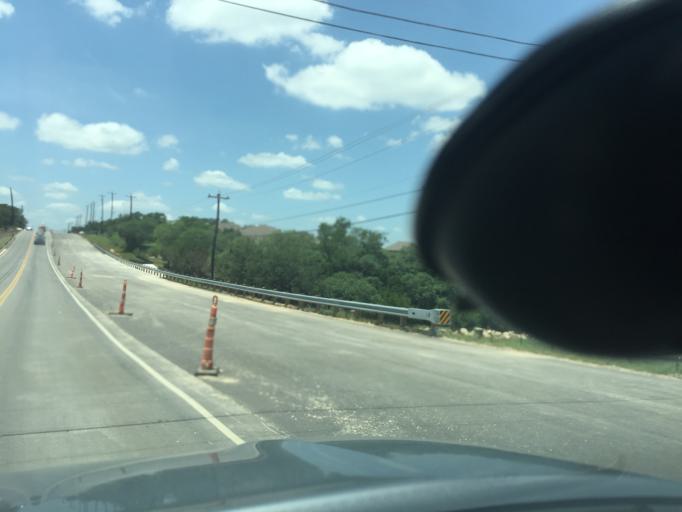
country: US
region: Texas
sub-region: Bexar County
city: Timberwood Park
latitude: 29.7081
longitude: -98.5052
